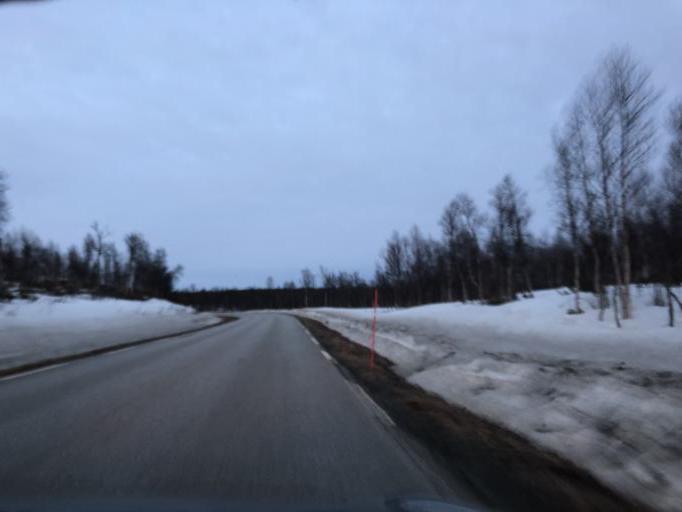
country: NO
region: Sor-Trondelag
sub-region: Tydal
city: Aas
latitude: 62.6997
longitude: 11.7930
